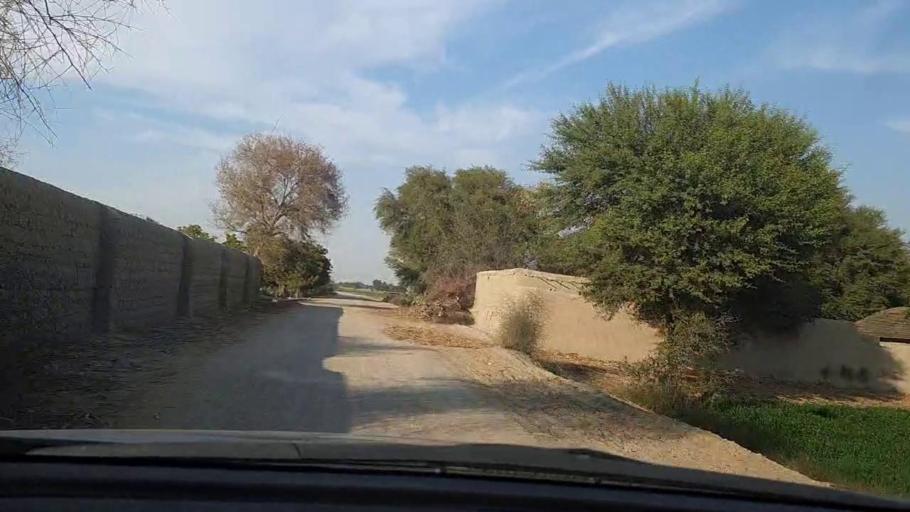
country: PK
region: Sindh
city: Daulatpur
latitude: 26.3232
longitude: 68.0265
